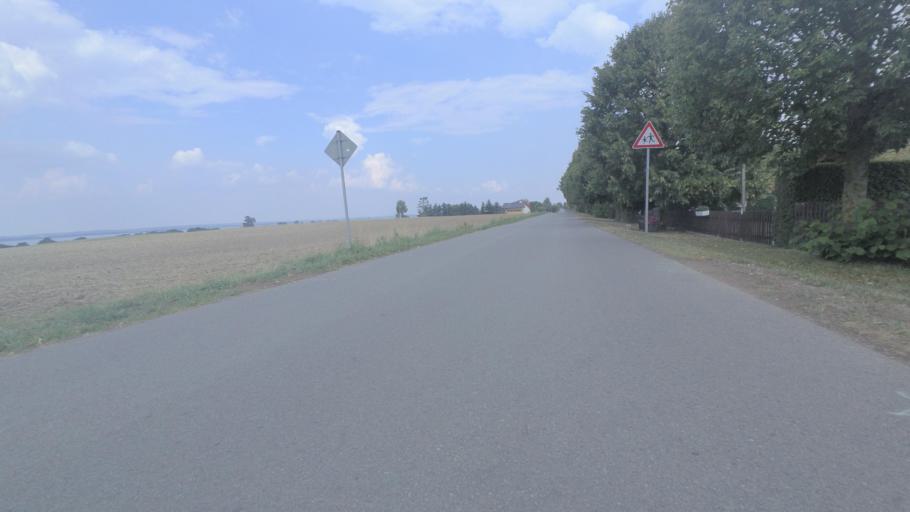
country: DE
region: Mecklenburg-Vorpommern
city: Borrentin
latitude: 53.7846
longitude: 12.8764
